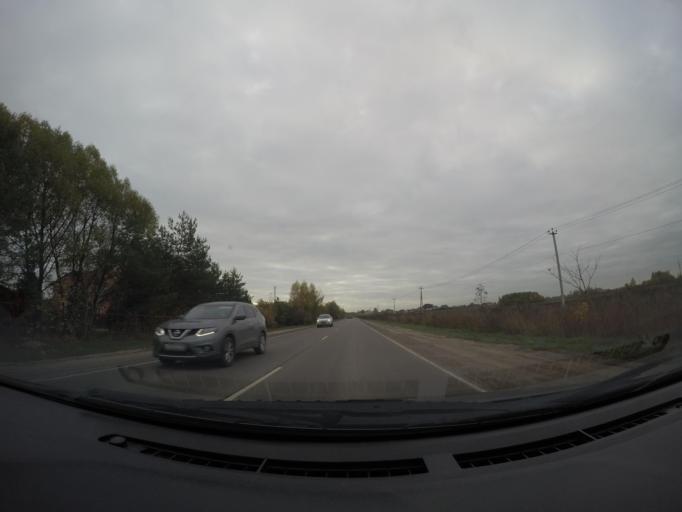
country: RU
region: Moskovskaya
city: Staraya Kupavna
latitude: 55.7702
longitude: 38.2007
